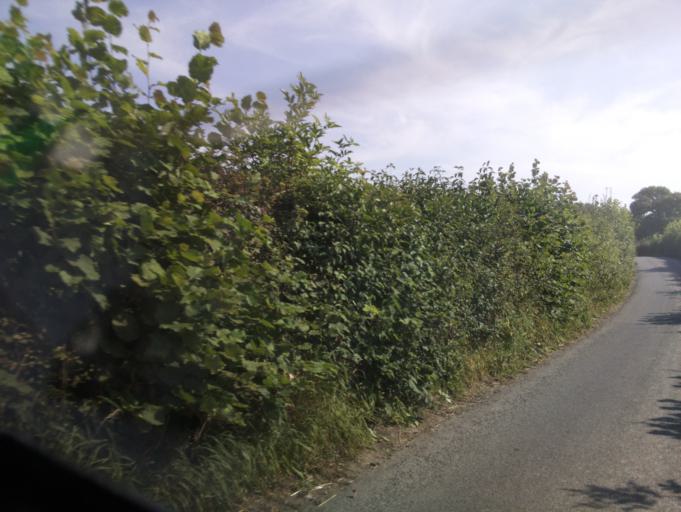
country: GB
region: England
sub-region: Gloucestershire
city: Dursley
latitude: 51.6970
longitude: -2.3160
